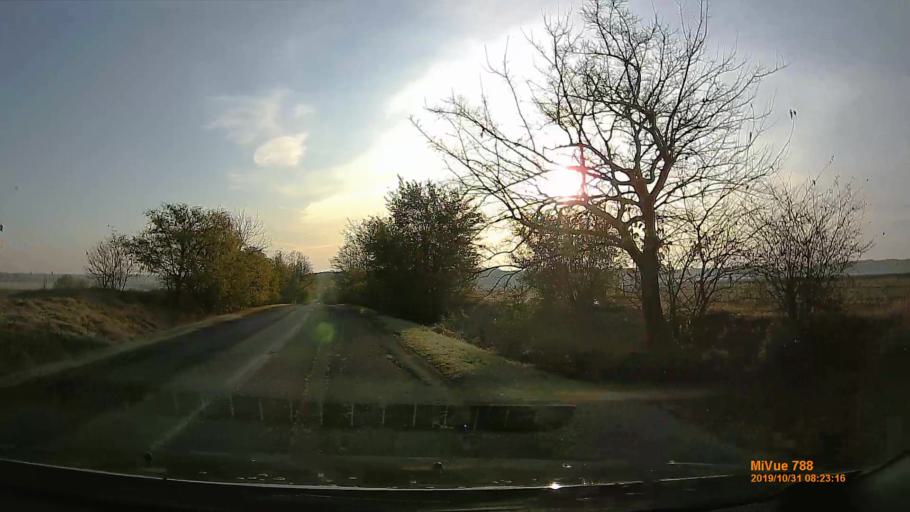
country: HU
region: Pest
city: Pand
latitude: 47.3688
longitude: 19.6425
